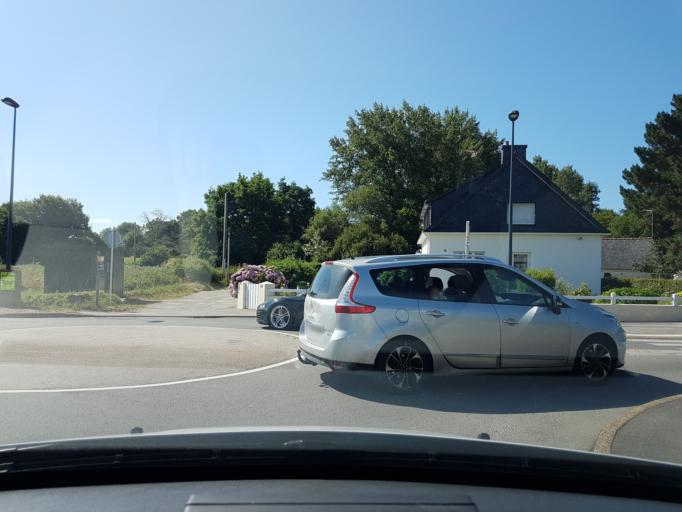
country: FR
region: Brittany
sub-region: Departement du Morbihan
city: Belz
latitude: 47.6759
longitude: -3.1803
